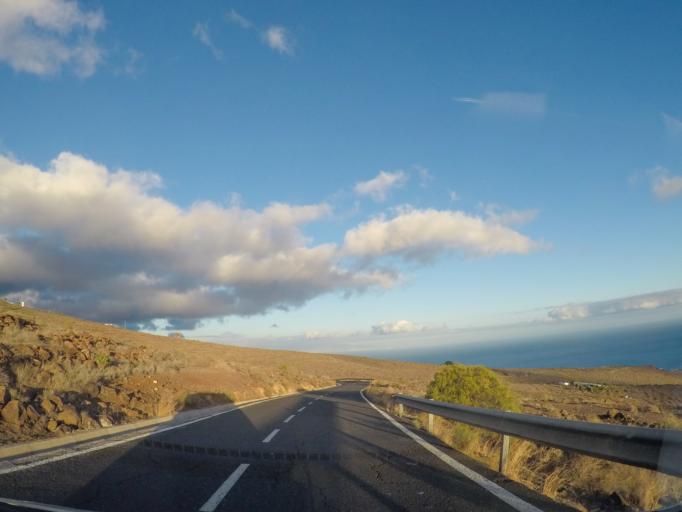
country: ES
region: Canary Islands
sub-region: Provincia de Santa Cruz de Tenerife
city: Alajero
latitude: 28.0398
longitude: -17.2328
